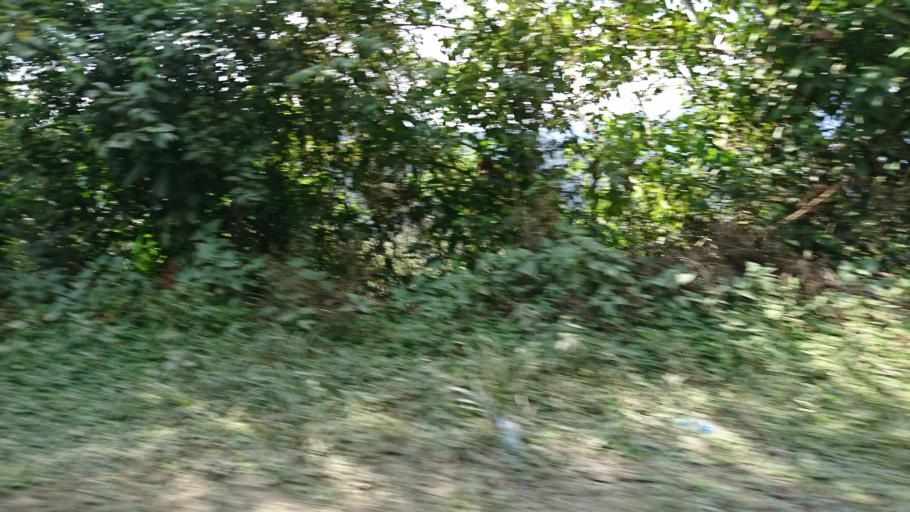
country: BO
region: La Paz
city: Coroico
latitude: -16.1306
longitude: -67.7515
